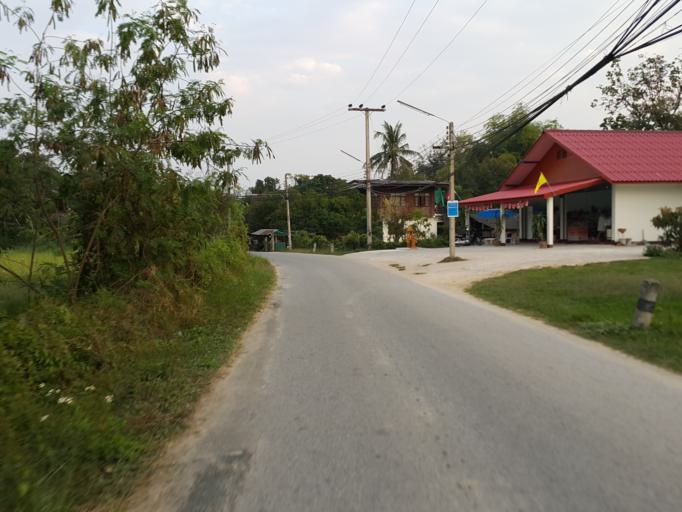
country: TH
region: Chiang Mai
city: San Sai
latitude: 18.8444
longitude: 99.0983
